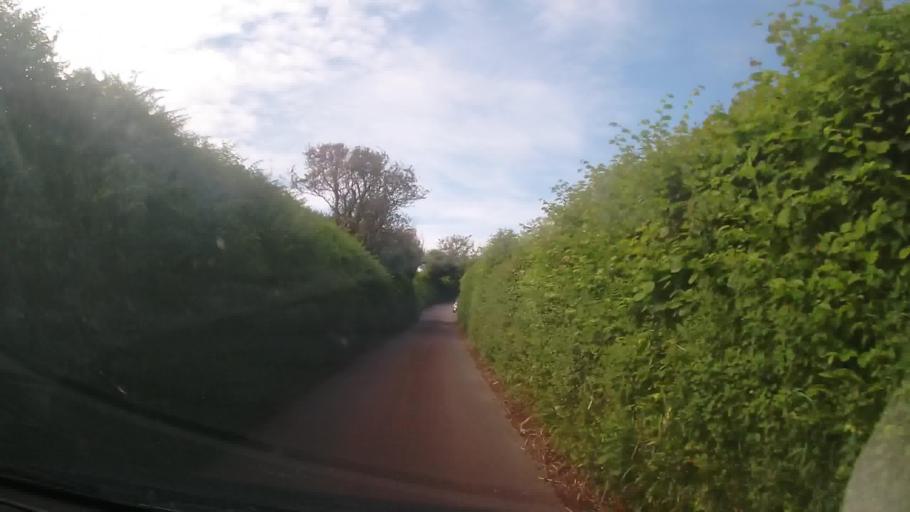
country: GB
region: England
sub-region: Devon
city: Salcombe
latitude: 50.2405
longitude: -3.6789
